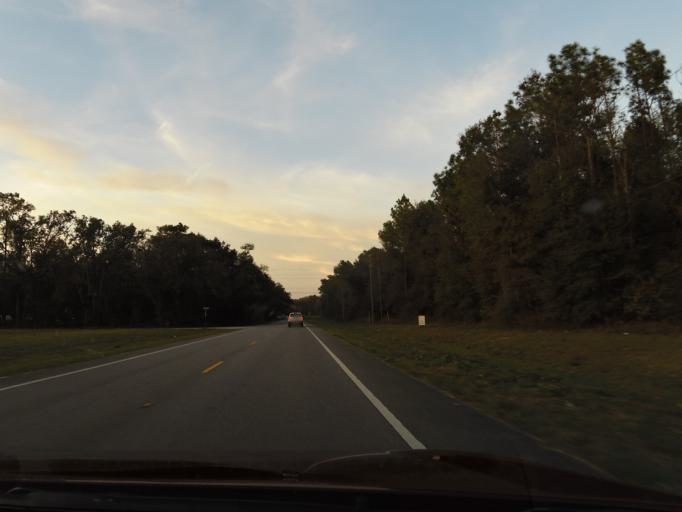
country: US
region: Florida
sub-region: Volusia County
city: De Leon Springs
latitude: 29.1372
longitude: -81.2848
